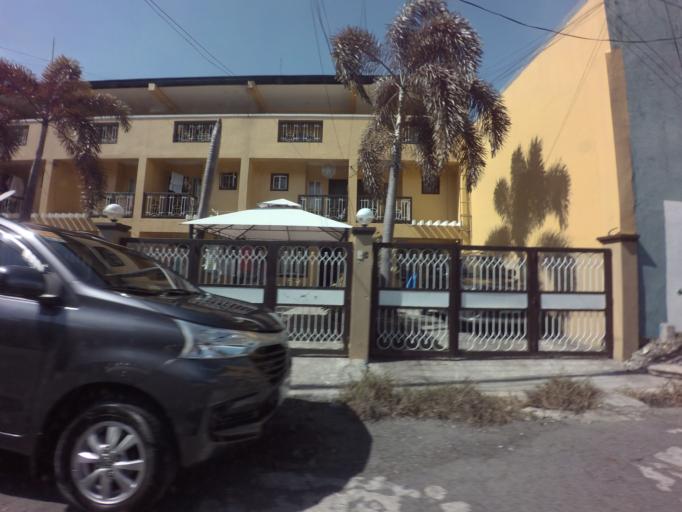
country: PH
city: Sambayanihan People's Village
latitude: 14.4435
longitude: 120.9941
